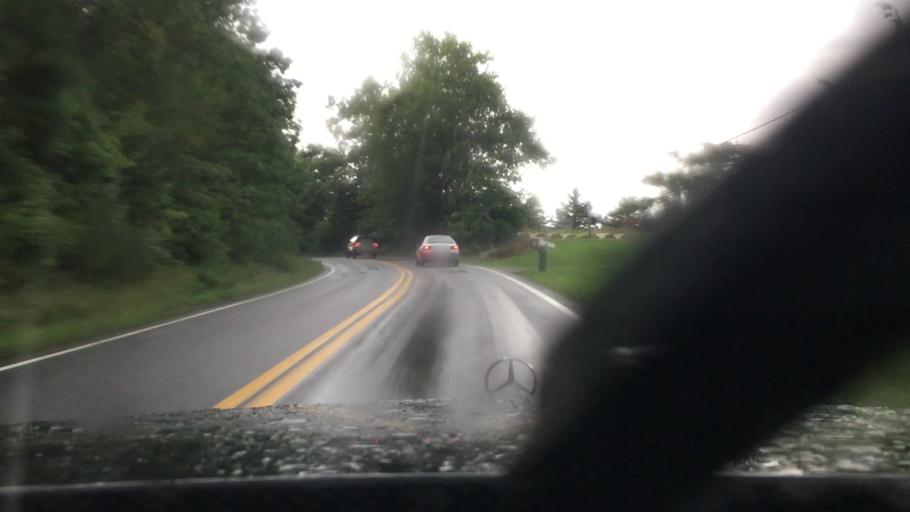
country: US
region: Virginia
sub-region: Campbell County
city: Timberlake
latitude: 37.2787
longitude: -79.2515
